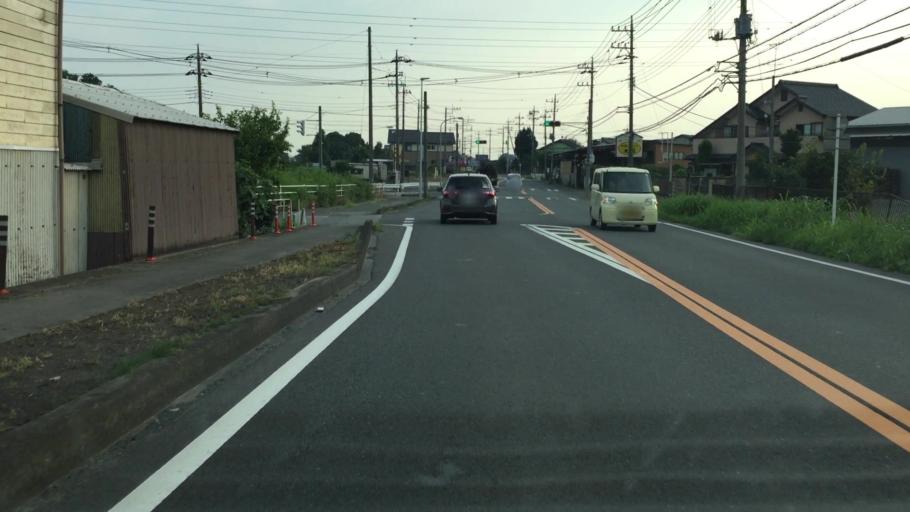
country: JP
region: Tochigi
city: Fujioka
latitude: 36.2809
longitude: 139.6622
